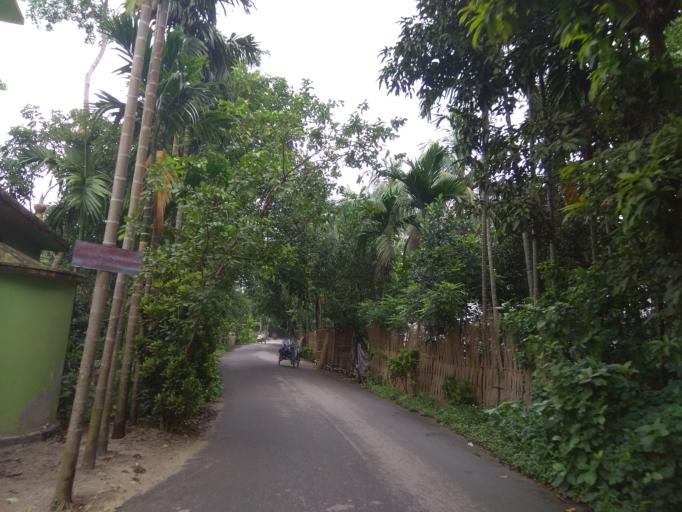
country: BD
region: Dhaka
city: Dohar
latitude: 23.4320
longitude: 90.0725
